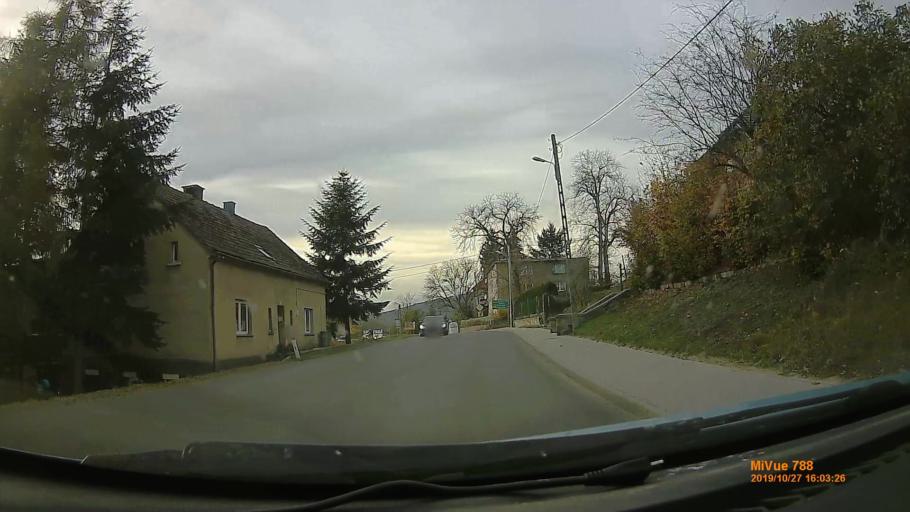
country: PL
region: Lower Silesian Voivodeship
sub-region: Powiat klodzki
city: Nowa Ruda
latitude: 50.5210
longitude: 16.4975
